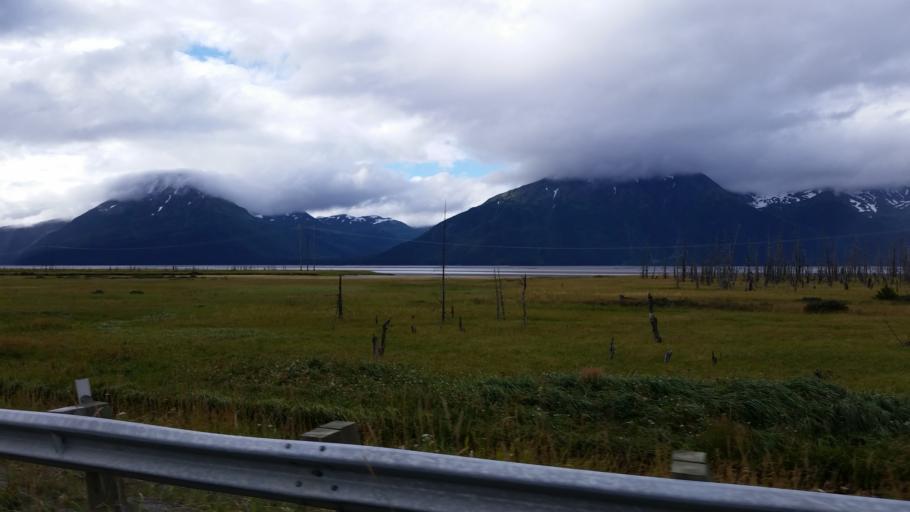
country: US
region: Alaska
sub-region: Anchorage Municipality
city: Girdwood
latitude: 60.9404
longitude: -149.1738
